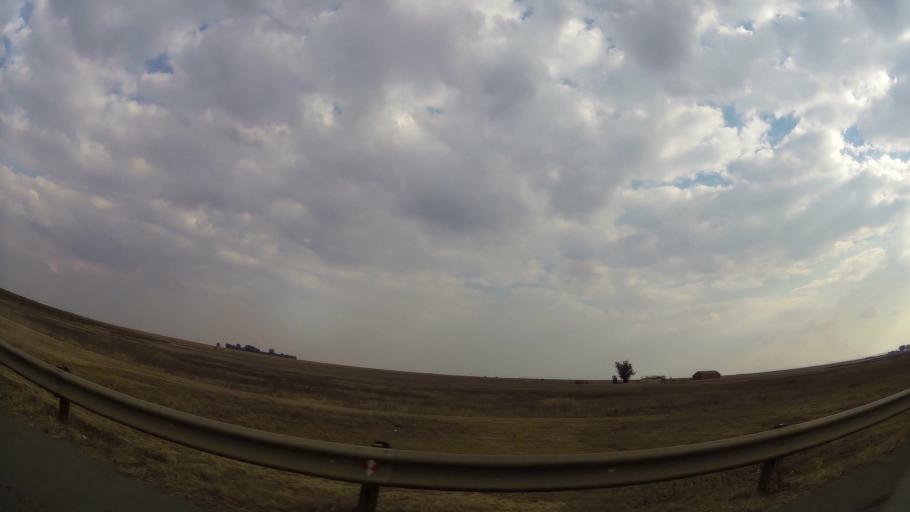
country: ZA
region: Gauteng
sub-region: Ekurhuleni Metropolitan Municipality
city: Nigel
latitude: -26.3177
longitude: 28.5873
